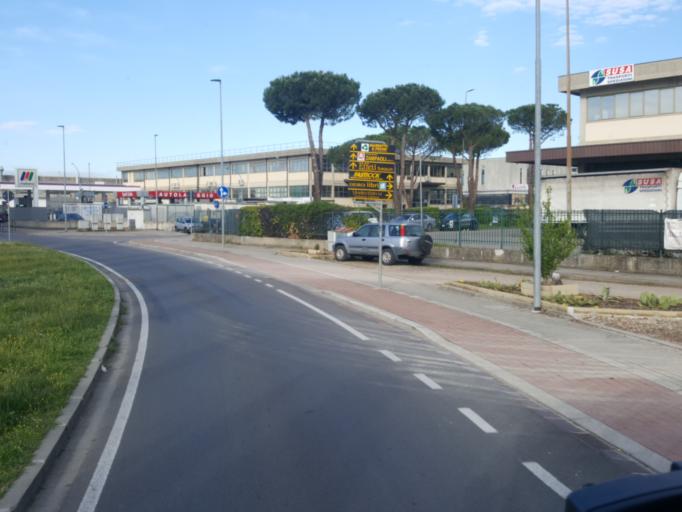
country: IT
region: Tuscany
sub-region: Province of Florence
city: Calenzano
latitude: 43.8414
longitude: 11.1769
